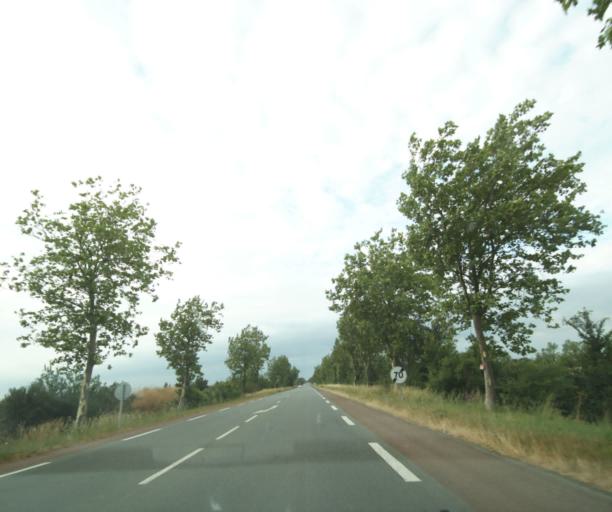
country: FR
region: Poitou-Charentes
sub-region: Departement de la Charente-Maritime
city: Marans
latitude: 46.2872
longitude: -0.9931
